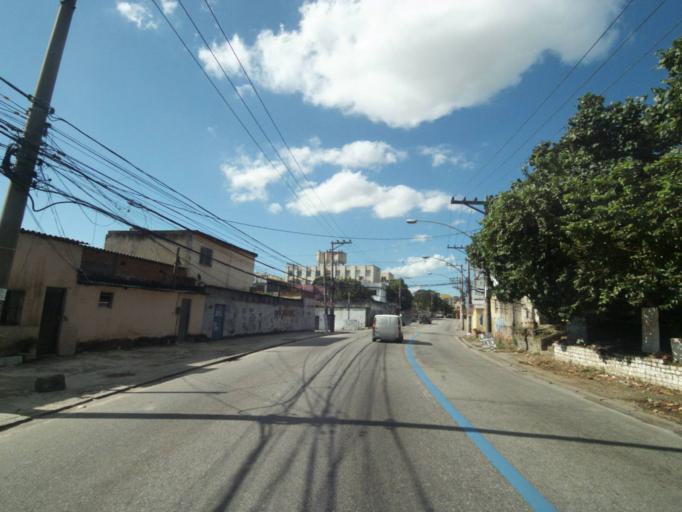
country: BR
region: Rio de Janeiro
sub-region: Rio De Janeiro
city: Rio de Janeiro
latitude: -22.9042
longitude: -43.2637
